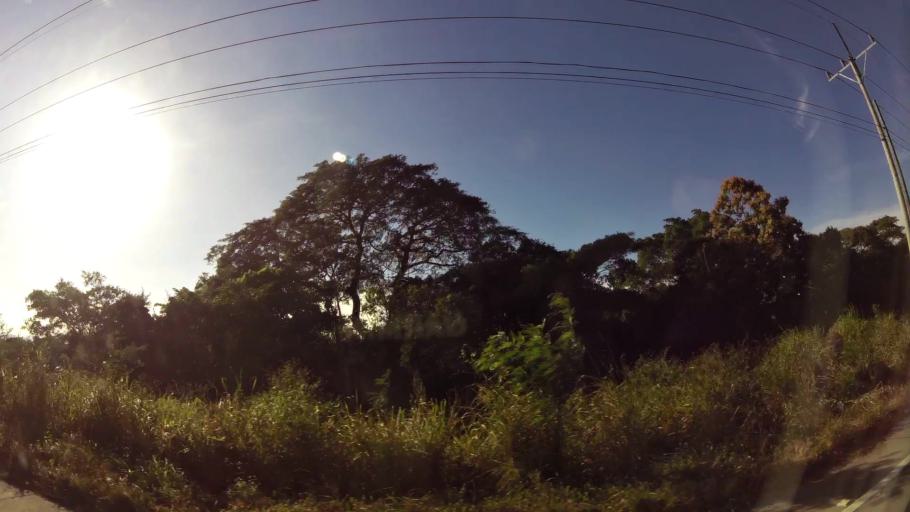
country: SV
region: Santa Ana
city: Metapan
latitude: 14.2595
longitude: -89.4605
